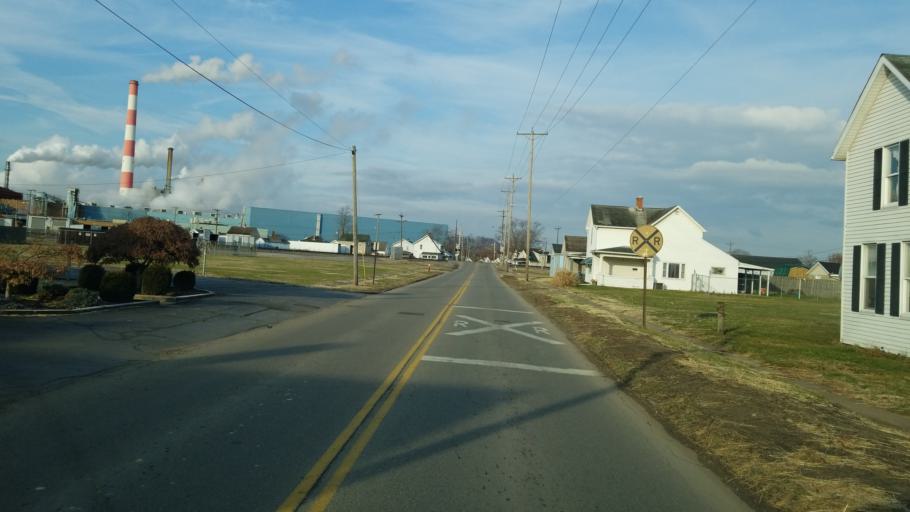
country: US
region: Ohio
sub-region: Ross County
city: Chillicothe
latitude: 39.3257
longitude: -82.9656
